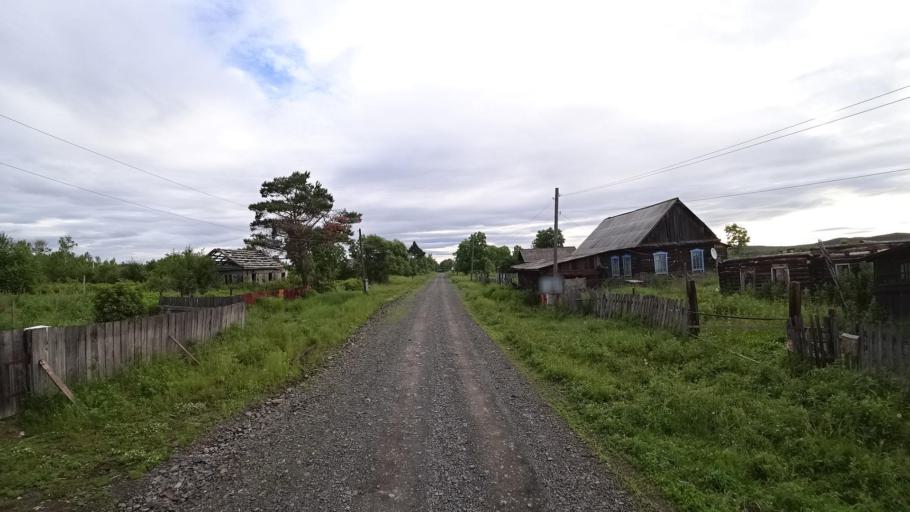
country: RU
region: Khabarovsk Krai
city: Amursk
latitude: 49.8879
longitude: 136.1287
